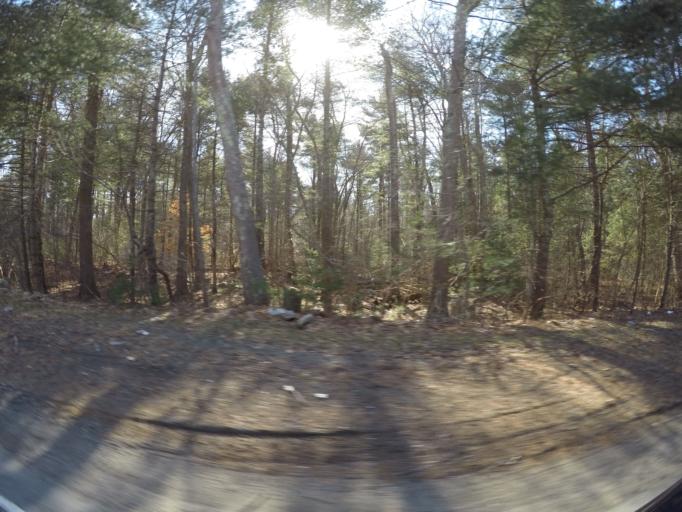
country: US
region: Massachusetts
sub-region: Plymouth County
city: Brockton
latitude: 42.0688
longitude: -71.0760
